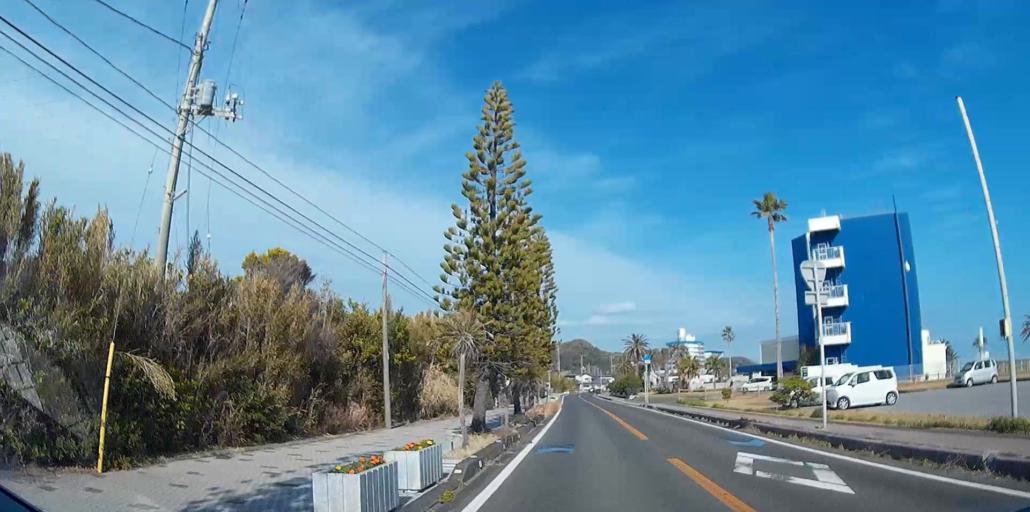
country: JP
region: Chiba
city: Tateyama
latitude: 34.9054
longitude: 139.8906
